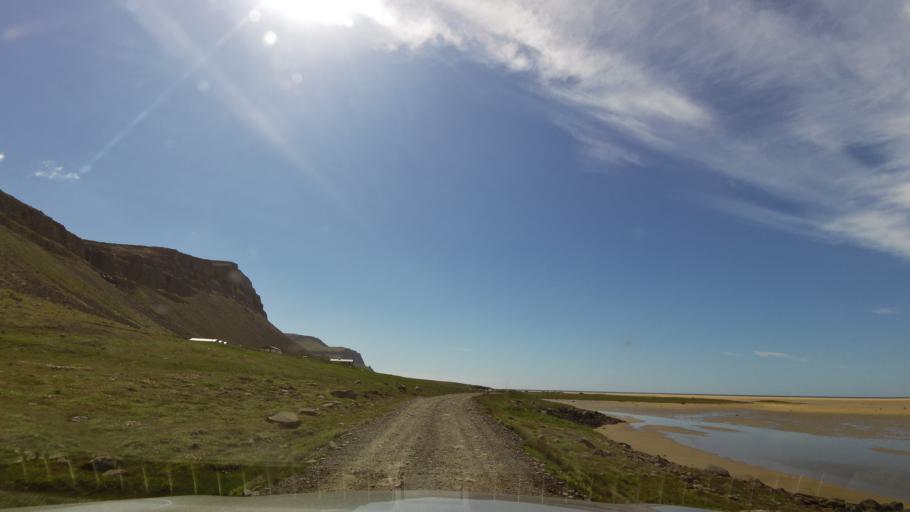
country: IS
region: West
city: Olafsvik
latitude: 65.4497
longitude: -23.9489
